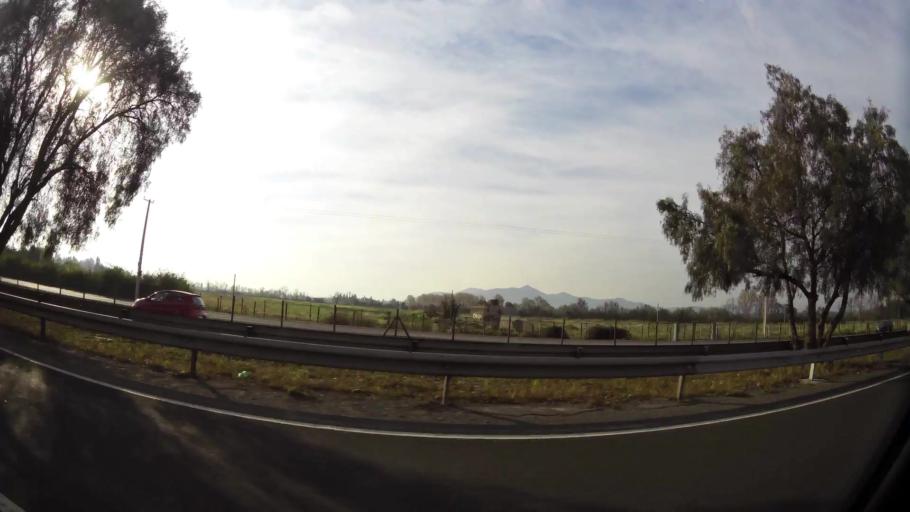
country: CL
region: Santiago Metropolitan
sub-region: Provincia de Talagante
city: Penaflor
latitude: -33.6181
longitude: -70.8572
